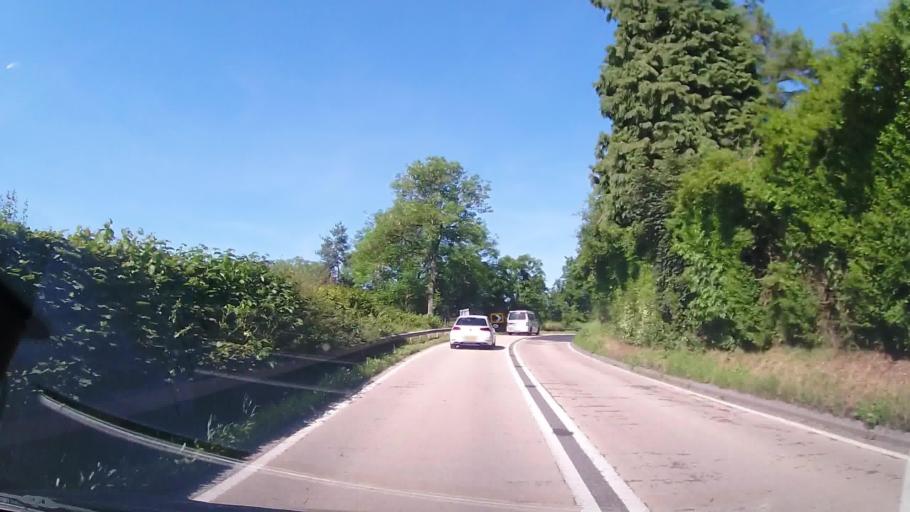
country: GB
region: Wales
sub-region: Sir Powys
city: Llanfyllin
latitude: 52.6639
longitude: -3.2915
